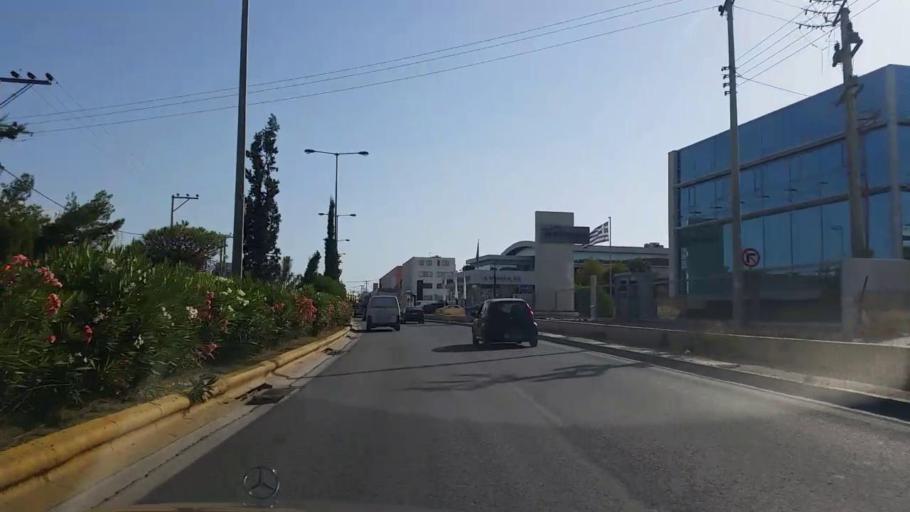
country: GR
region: Attica
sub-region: Nomarchia Anatolikis Attikis
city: Koropi
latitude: 37.8800
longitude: 23.8711
